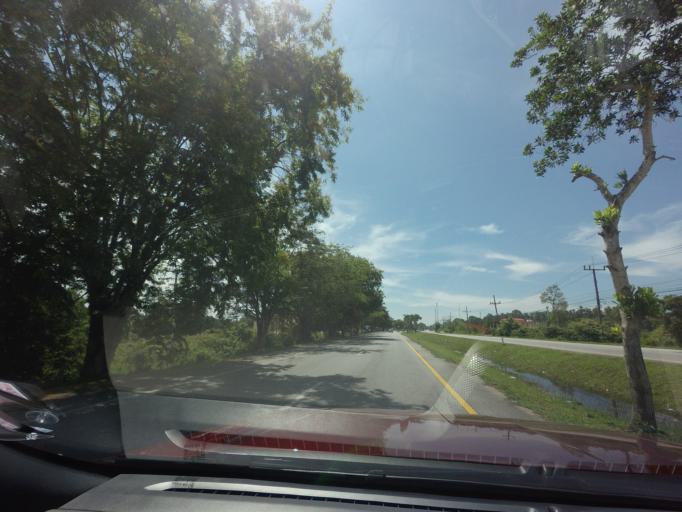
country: TH
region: Pattani
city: Mai Kaen
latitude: 6.5997
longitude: 101.6323
